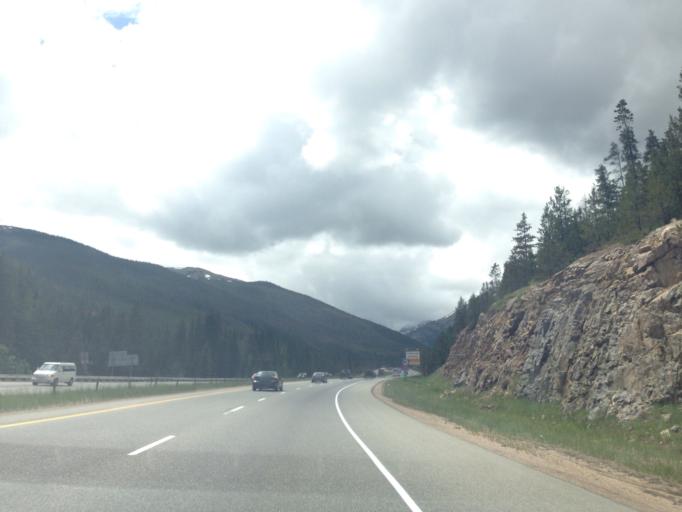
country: US
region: Colorado
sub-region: Clear Creek County
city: Georgetown
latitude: 39.6919
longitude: -105.8100
